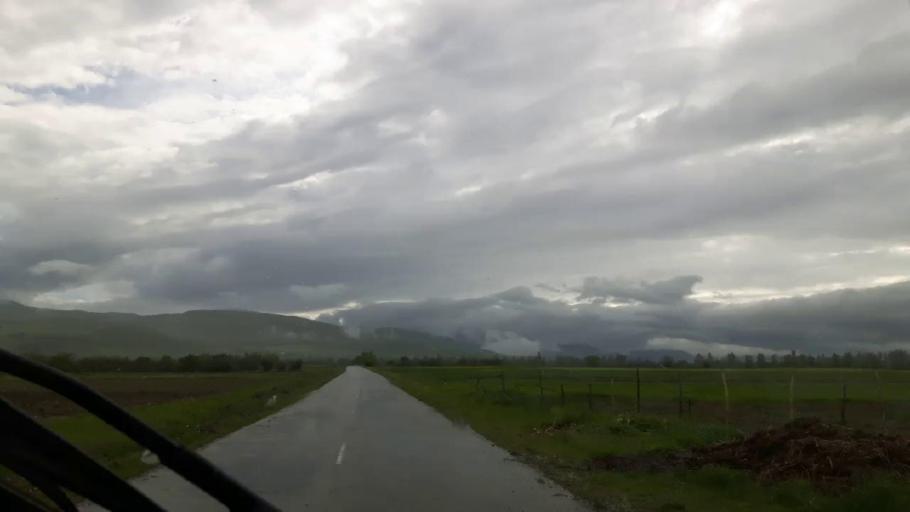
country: GE
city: Agara
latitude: 41.9994
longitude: 43.7514
